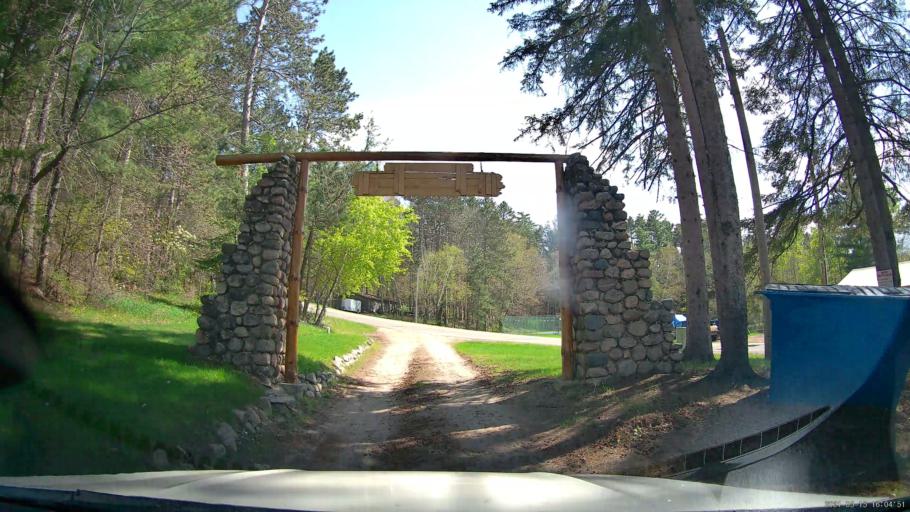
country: US
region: Minnesota
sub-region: Hubbard County
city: Park Rapids
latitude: 46.9866
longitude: -94.9510
